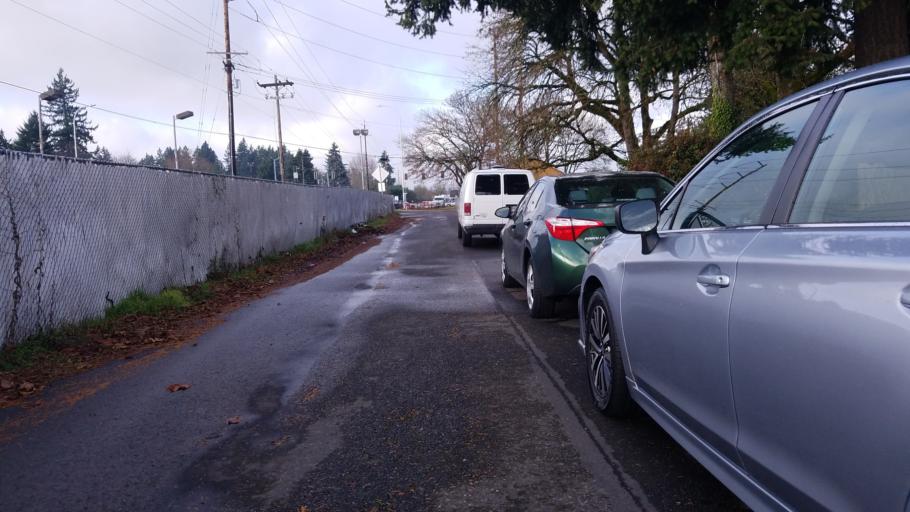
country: US
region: Oregon
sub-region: Clackamas County
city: Jennings Lodge
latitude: 45.3907
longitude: -122.6117
